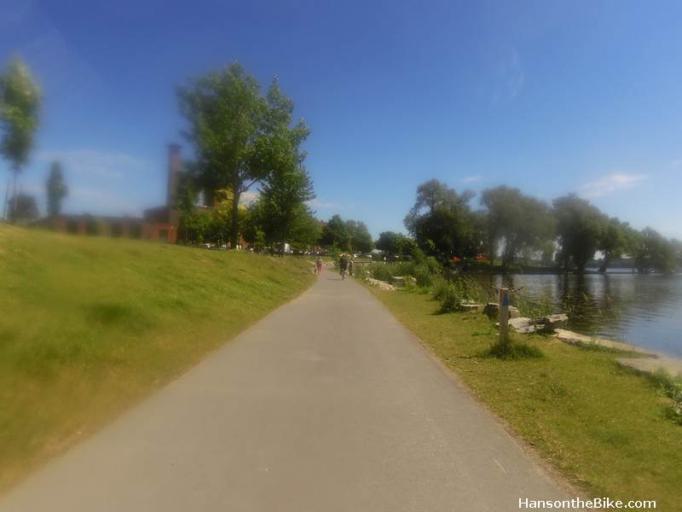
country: CA
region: Ontario
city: Kingston
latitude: 44.2405
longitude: -76.4812
